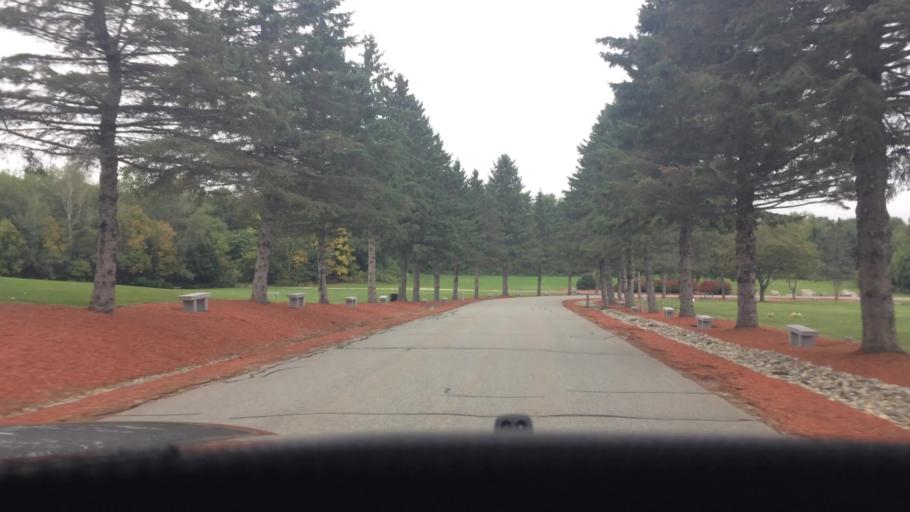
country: US
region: Maine
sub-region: Kennebec County
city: Augusta
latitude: 44.3526
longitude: -69.7877
